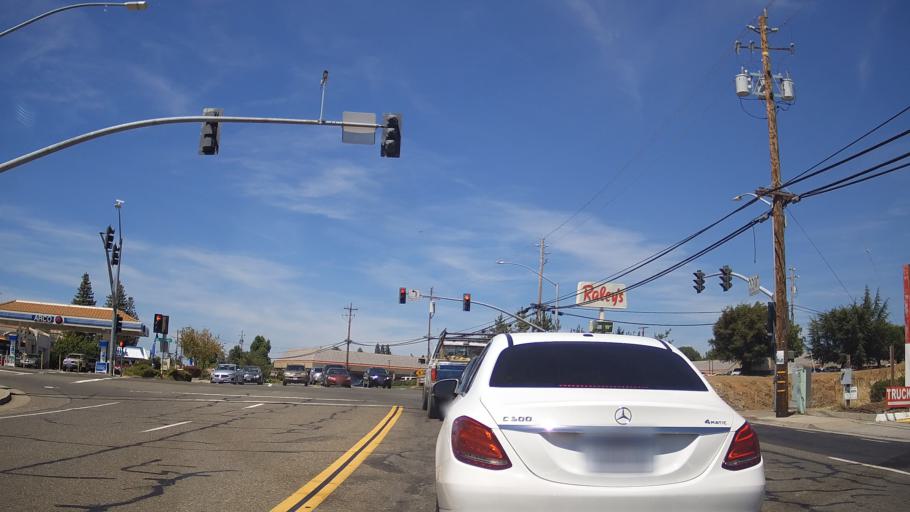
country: US
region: California
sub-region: Placer County
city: North Auburn
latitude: 38.9229
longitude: -121.0562
